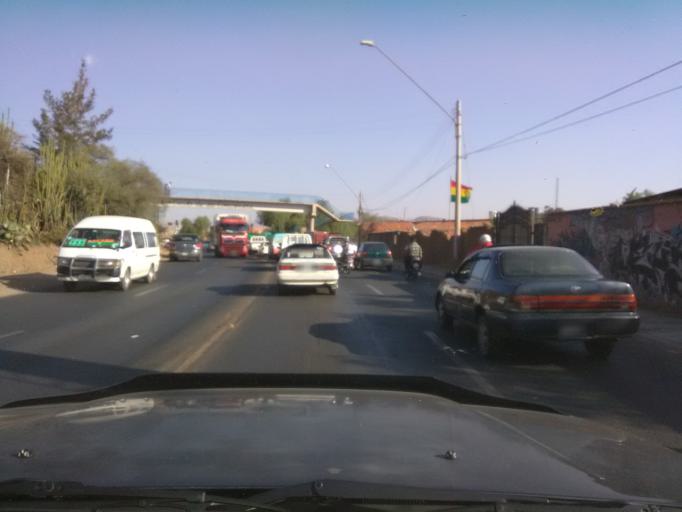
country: BO
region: Cochabamba
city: Cochabamba
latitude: -17.3880
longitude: -66.1409
